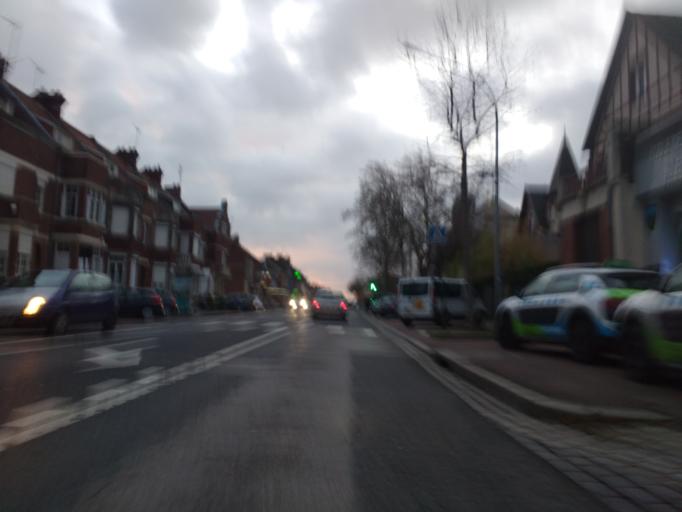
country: FR
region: Picardie
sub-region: Departement de la Somme
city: Rivery
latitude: 49.8841
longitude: 2.3233
